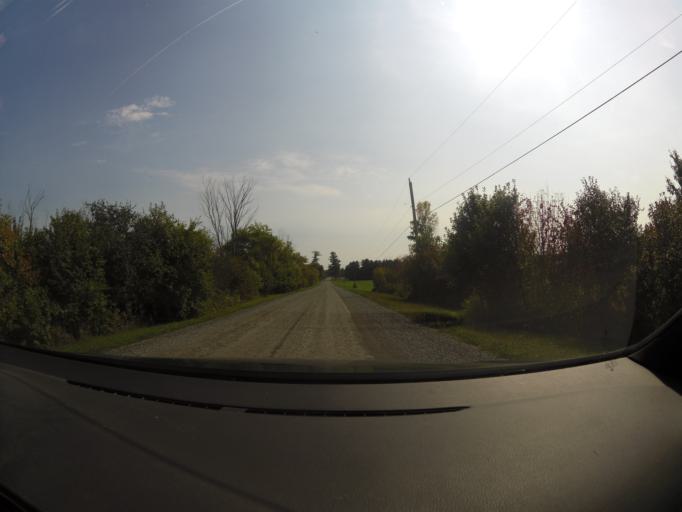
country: CA
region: Ontario
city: Arnprior
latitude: 45.3307
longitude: -76.1813
